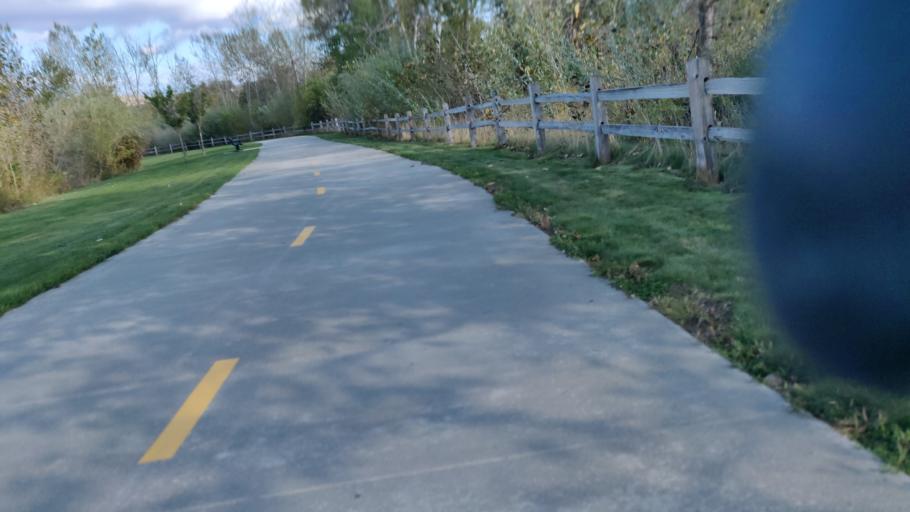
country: US
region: Idaho
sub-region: Ada County
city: Boise
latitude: 43.5713
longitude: -116.1422
